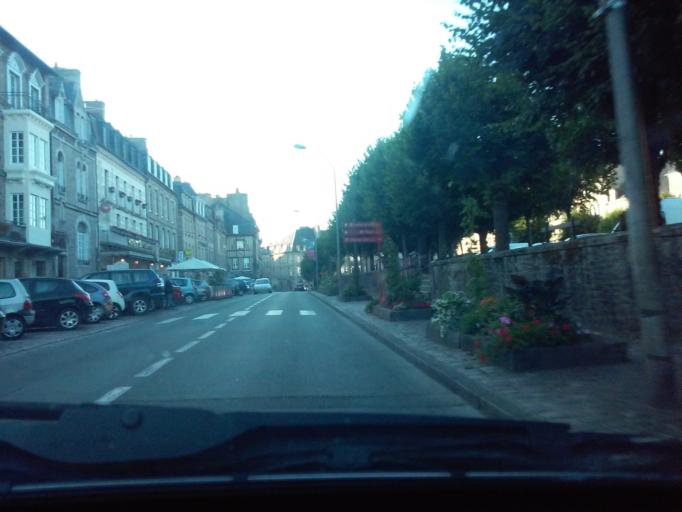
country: FR
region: Brittany
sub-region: Departement des Cotes-d'Armor
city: Lehon
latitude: 48.4515
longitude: -2.0444
